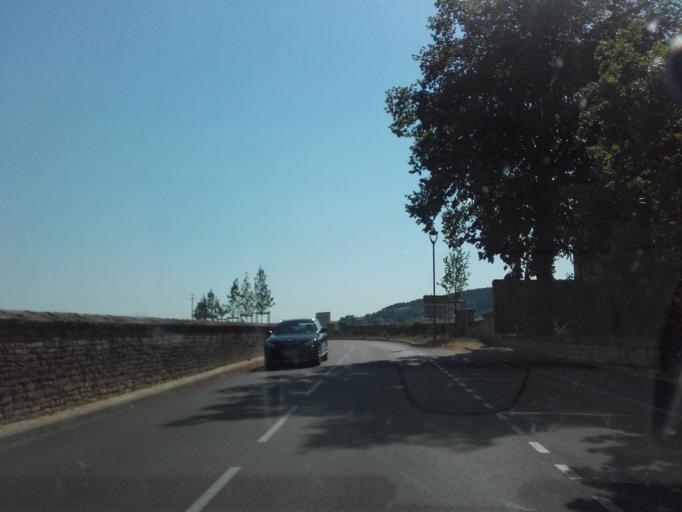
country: FR
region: Bourgogne
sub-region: Departement de la Cote-d'Or
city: Bligny-les-Beaune
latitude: 47.0070
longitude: 4.7954
